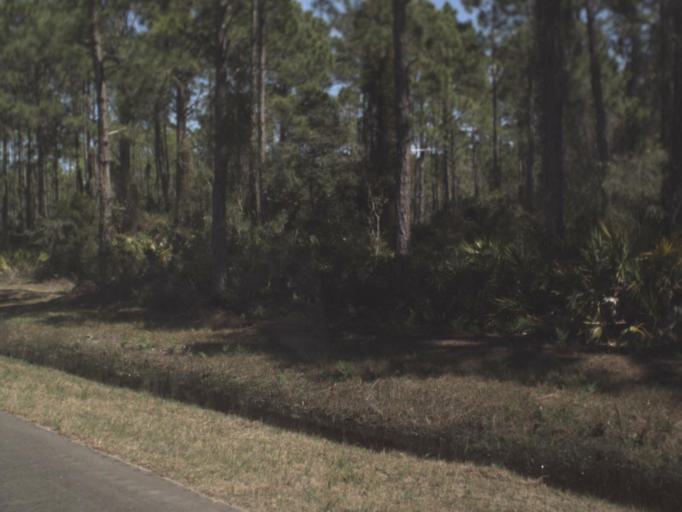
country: US
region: Florida
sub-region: Gulf County
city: Port Saint Joe
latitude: 29.7070
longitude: -85.3042
